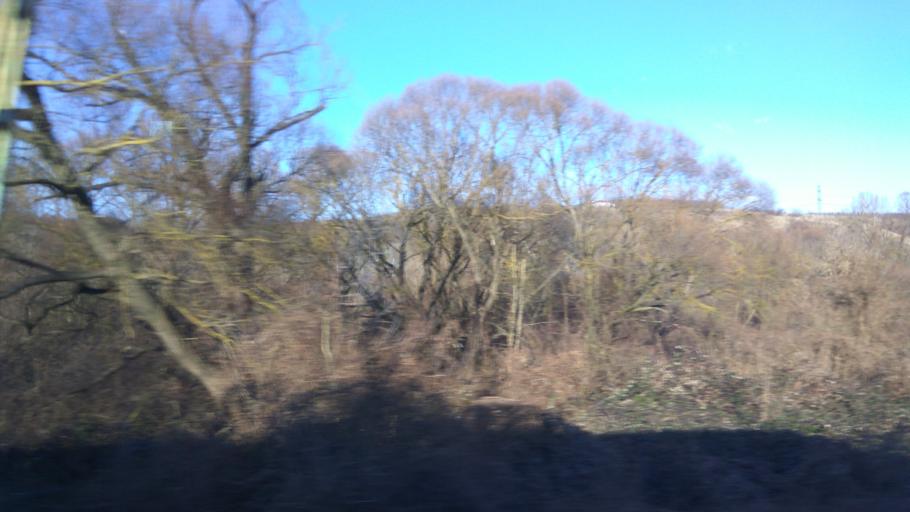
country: HU
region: Pest
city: Pecel
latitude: 47.4947
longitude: 19.3572
